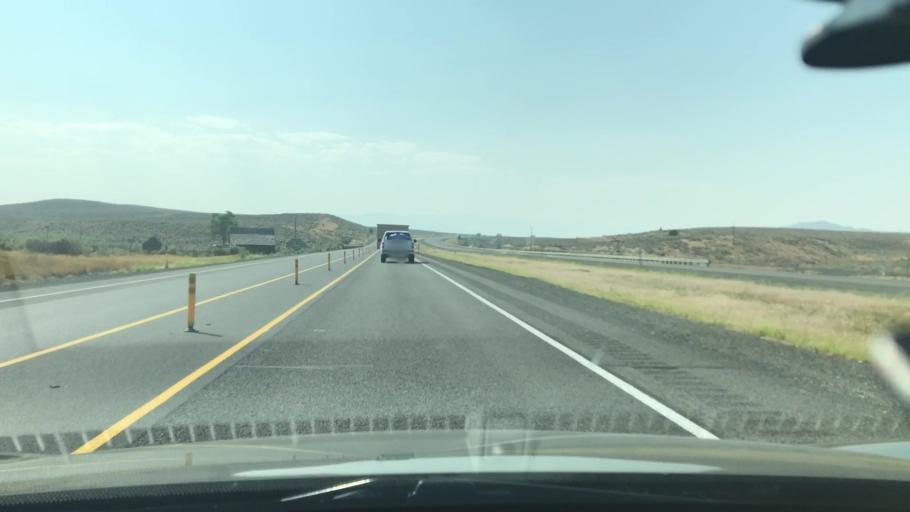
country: US
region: Oregon
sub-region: Baker County
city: Baker City
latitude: 44.6861
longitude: -117.6714
